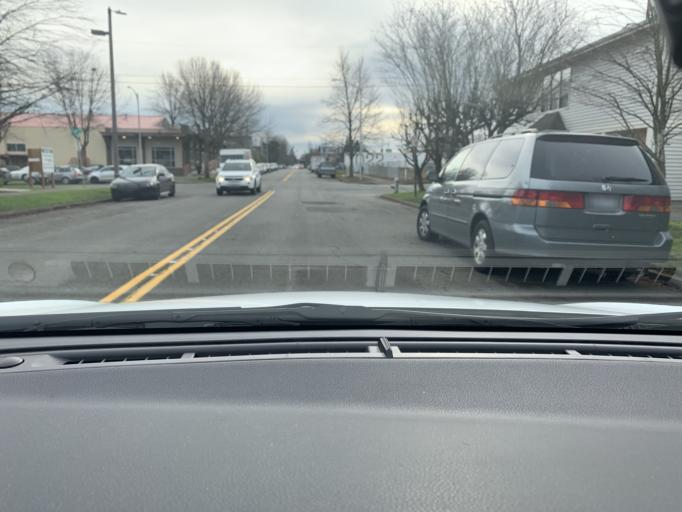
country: US
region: Washington
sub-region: Pierce County
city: Tacoma
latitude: 47.2537
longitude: -122.4507
